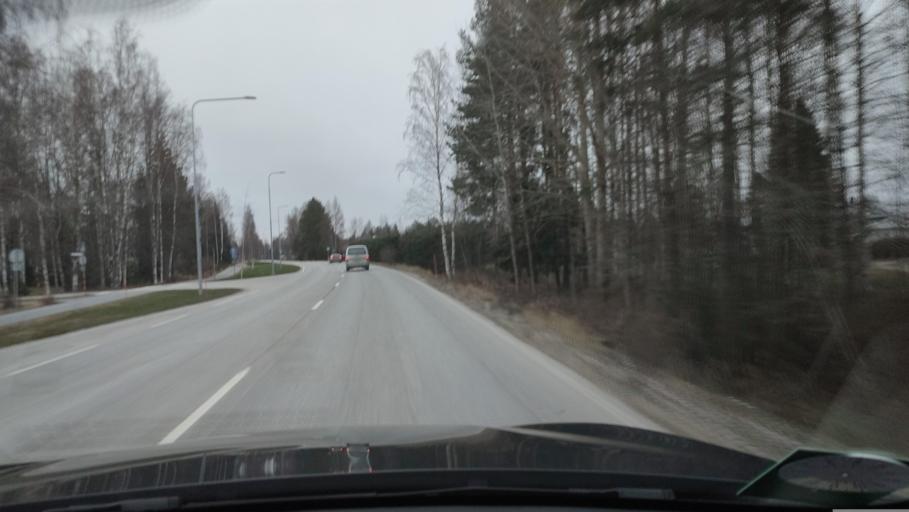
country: FI
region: Southern Ostrobothnia
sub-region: Suupohja
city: Kauhajoki
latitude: 62.4414
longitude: 22.1980
